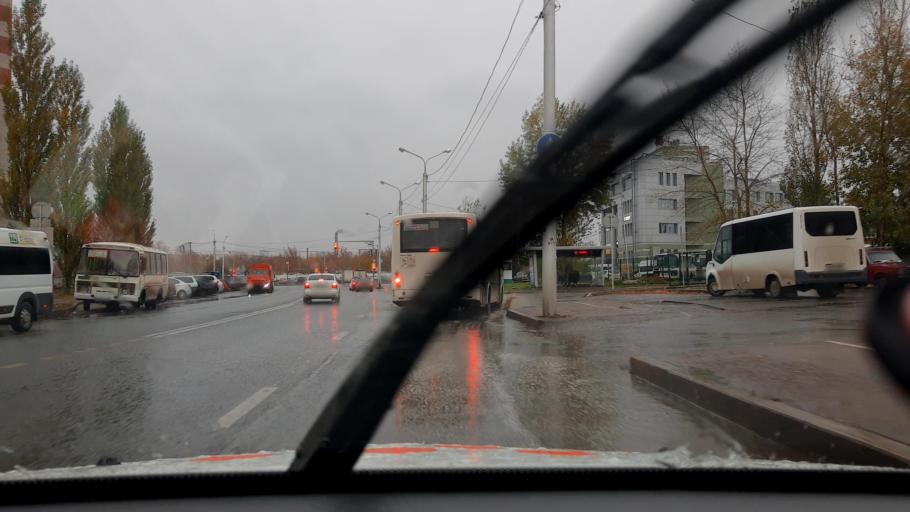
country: RU
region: Bashkortostan
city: Ufa
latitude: 54.7790
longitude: 56.0727
